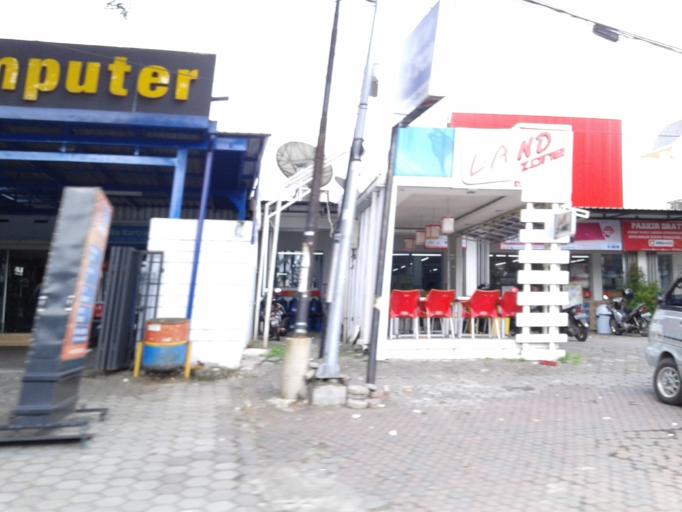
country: ID
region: East Java
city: Malang
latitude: -7.9657
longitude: 112.6200
